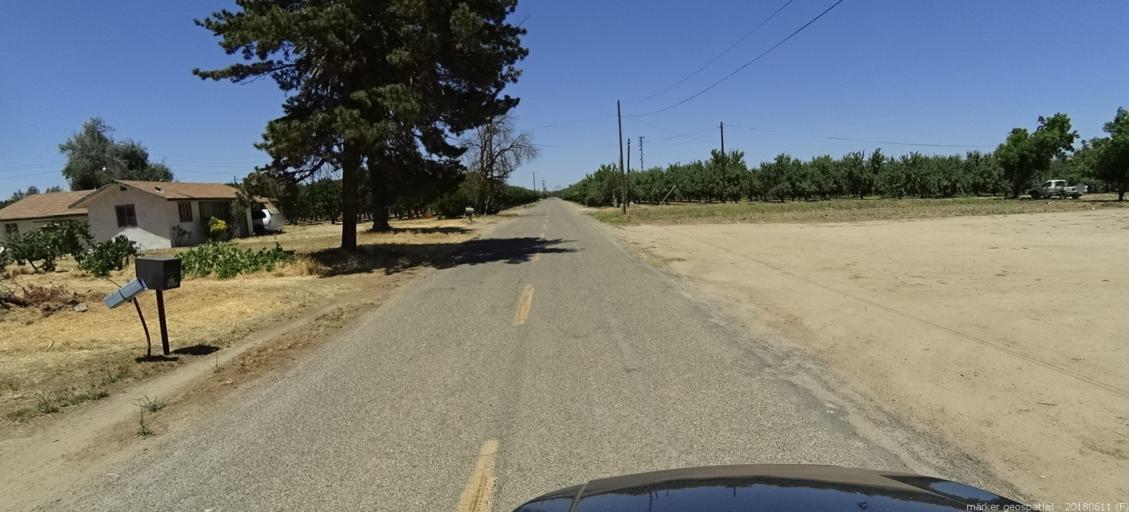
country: US
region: California
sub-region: Madera County
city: Fairmead
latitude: 37.0724
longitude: -120.2115
